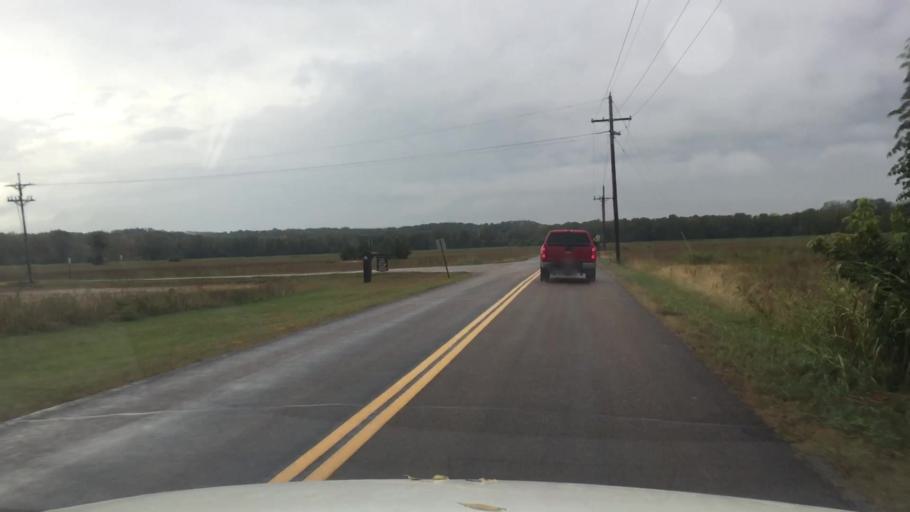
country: US
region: Missouri
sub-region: Boone County
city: Columbia
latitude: 38.8853
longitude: -92.4596
